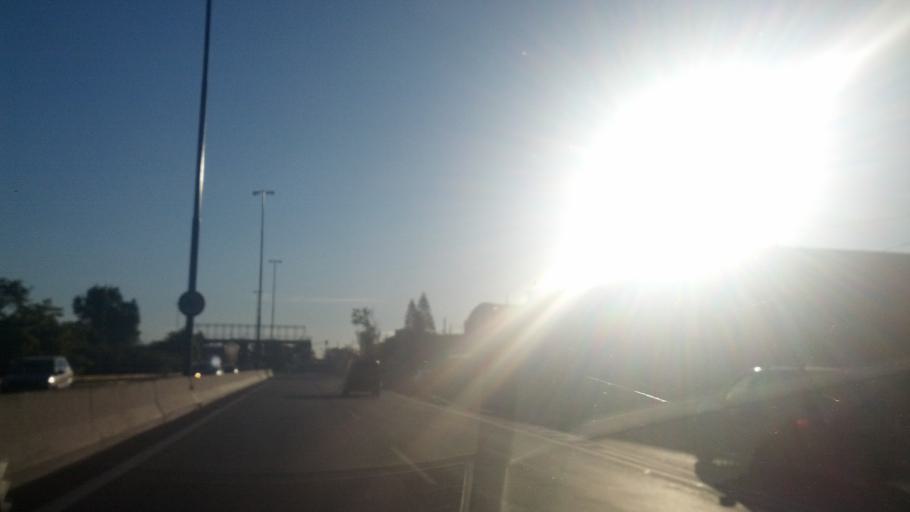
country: AR
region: Buenos Aires
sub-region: Partido de Lomas de Zamora
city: Lomas de Zamora
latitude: -34.7501
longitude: -58.4340
